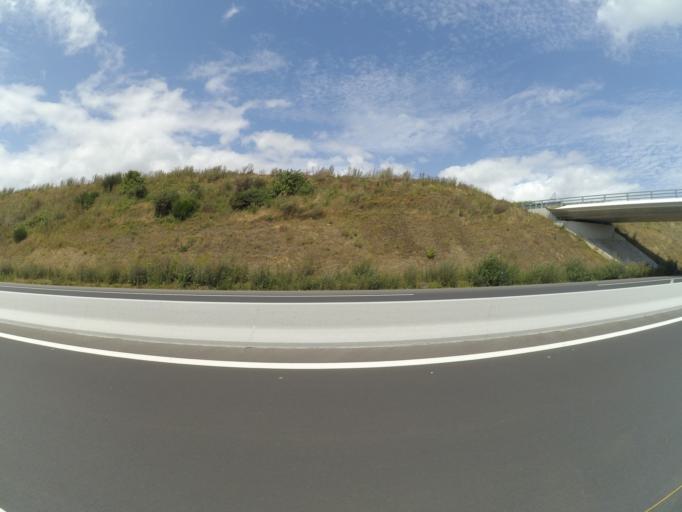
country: FR
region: Brittany
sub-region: Departement des Cotes-d'Armor
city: Langueux
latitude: 48.4770
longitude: -2.7092
